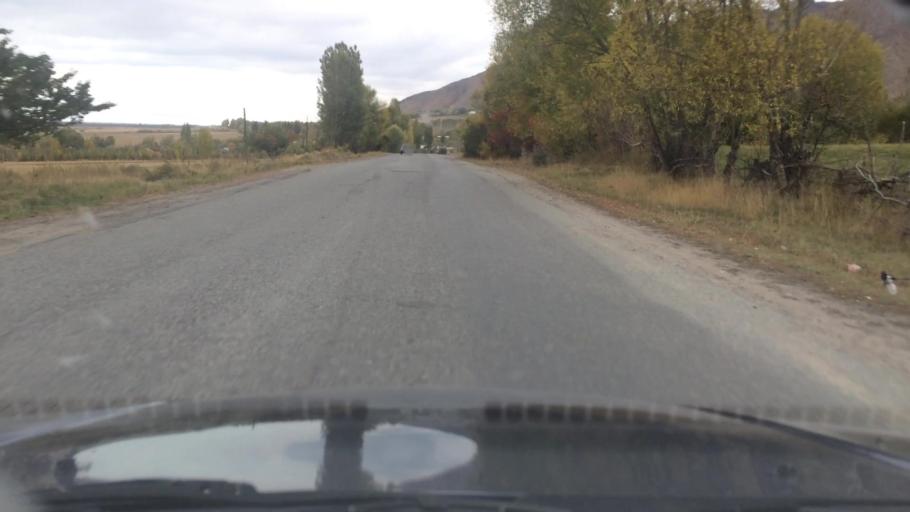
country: KG
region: Ysyk-Koel
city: Tyup
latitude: 42.7475
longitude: 78.0981
